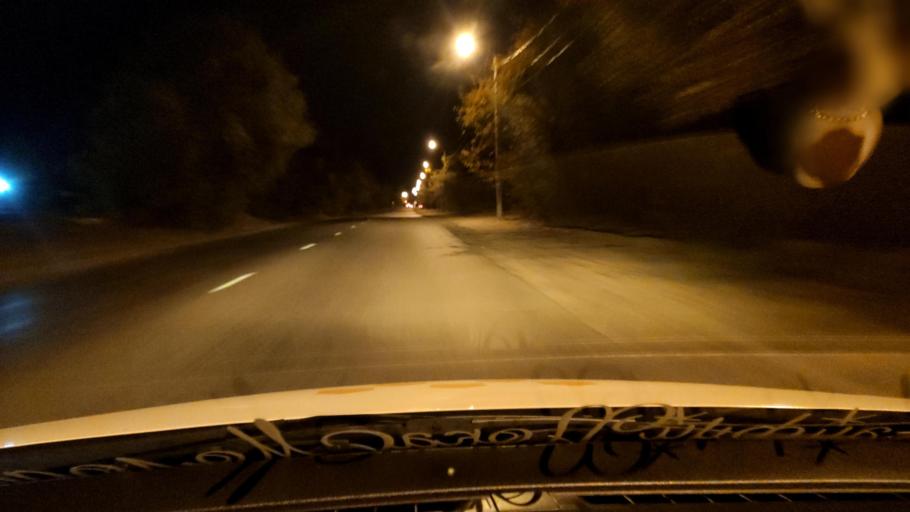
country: RU
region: Voronezj
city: Pridonskoy
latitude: 51.6856
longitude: 39.0995
